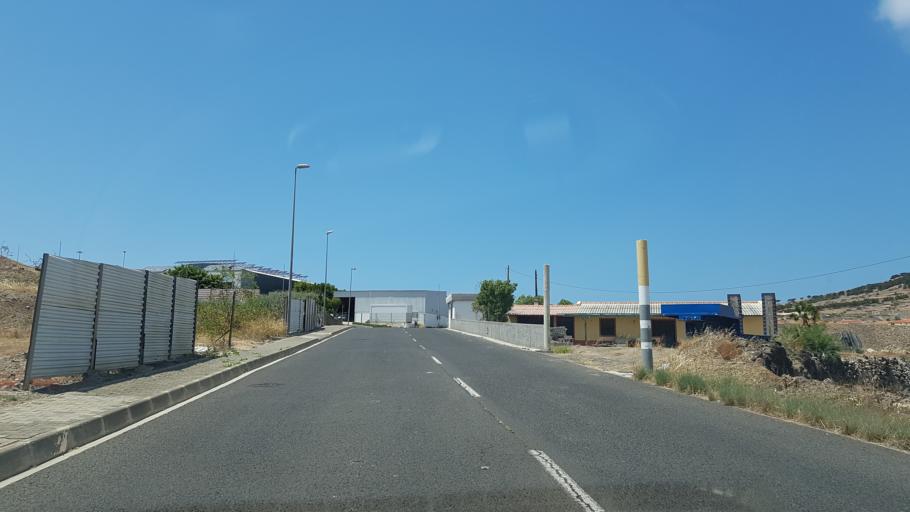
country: PT
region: Madeira
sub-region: Porto Santo
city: Vila de Porto Santo
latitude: 33.0684
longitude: -16.3420
